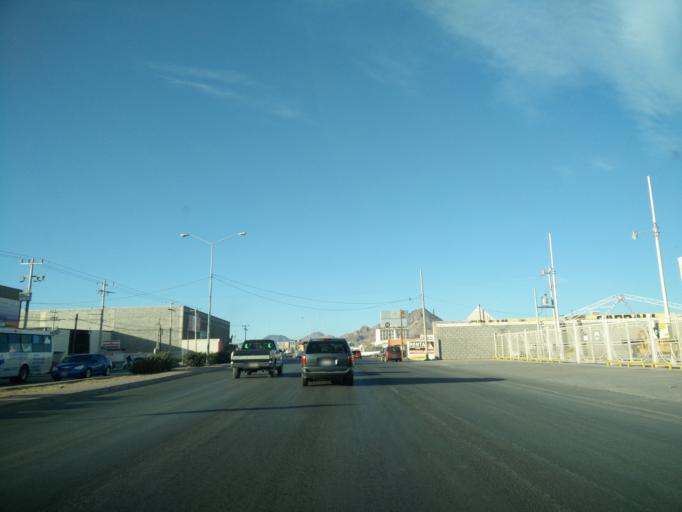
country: MX
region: Chihuahua
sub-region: Chihuahua
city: Chihuahua
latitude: 28.6353
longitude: -106.0197
